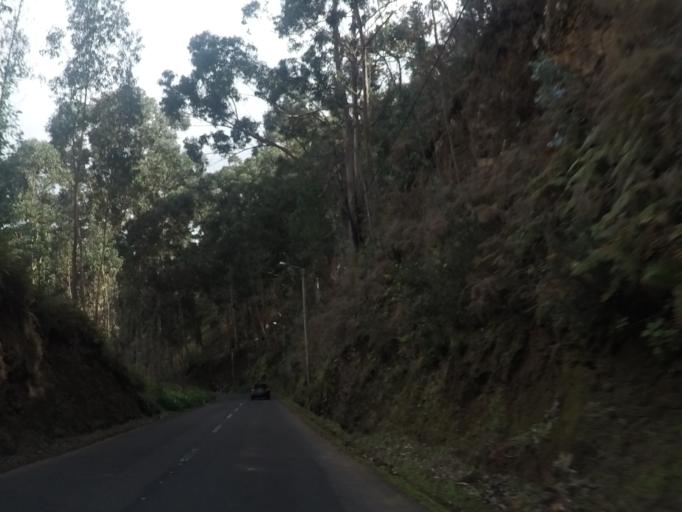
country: PT
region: Madeira
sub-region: Calheta
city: Faja da Ovelha
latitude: 32.8176
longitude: -17.2355
